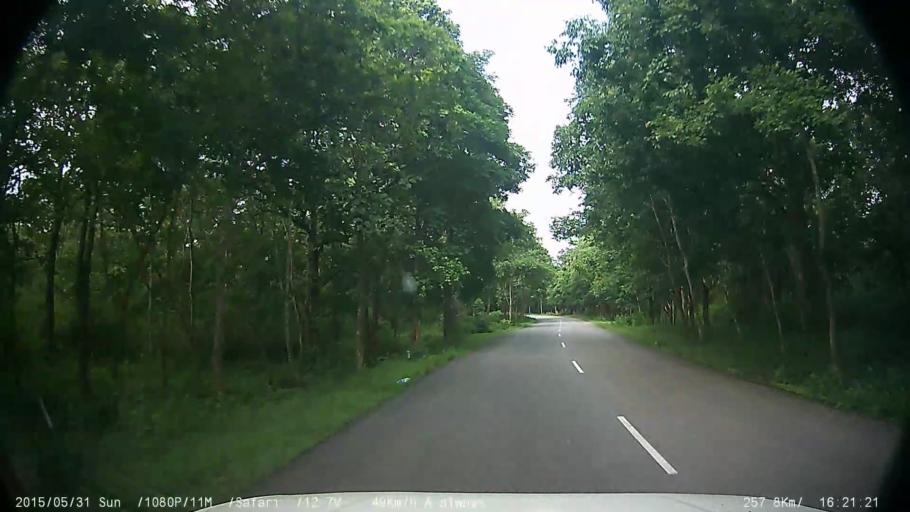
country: IN
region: Karnataka
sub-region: Chamrajnagar
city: Gundlupet
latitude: 11.7524
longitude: 76.5044
